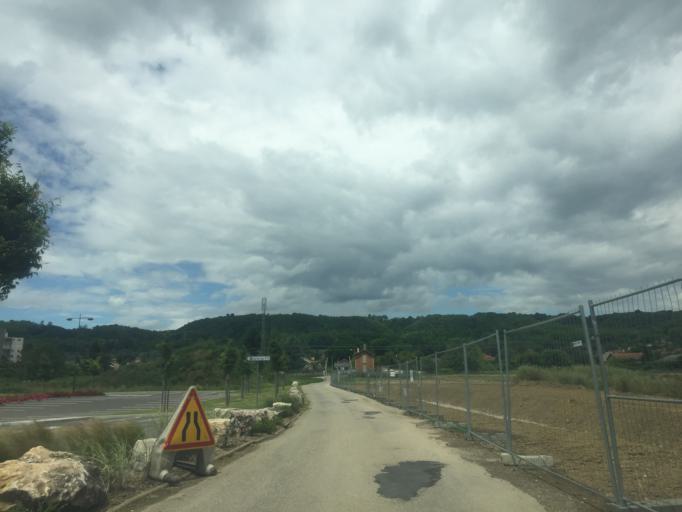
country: FR
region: Rhone-Alpes
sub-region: Departement de l'Ain
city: Saint-Maurice-de-Beynost
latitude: 45.8283
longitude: 4.9883
